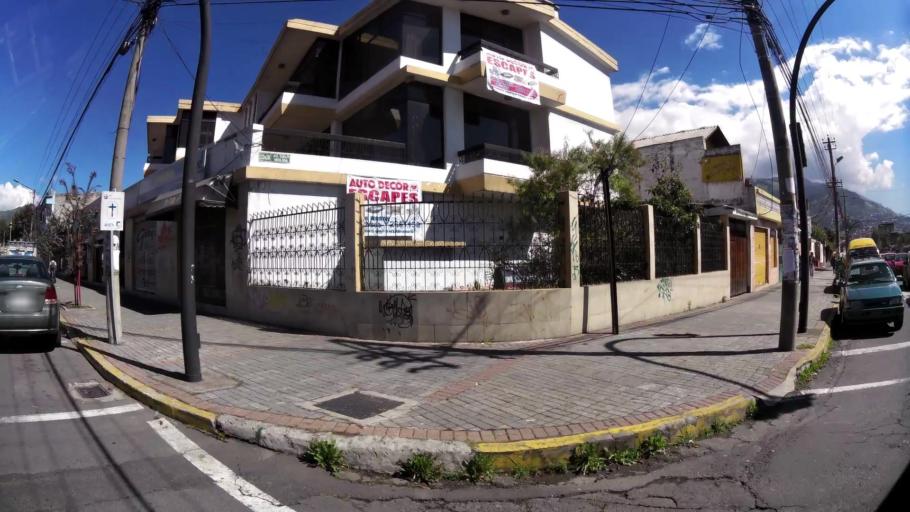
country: EC
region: Pichincha
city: Quito
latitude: -0.2476
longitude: -78.5295
